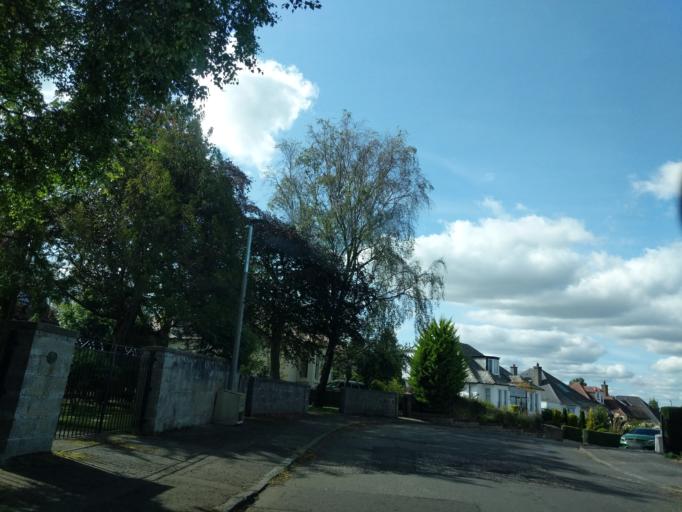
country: GB
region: Scotland
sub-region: Edinburgh
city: Colinton
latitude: 55.9099
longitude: -3.2665
